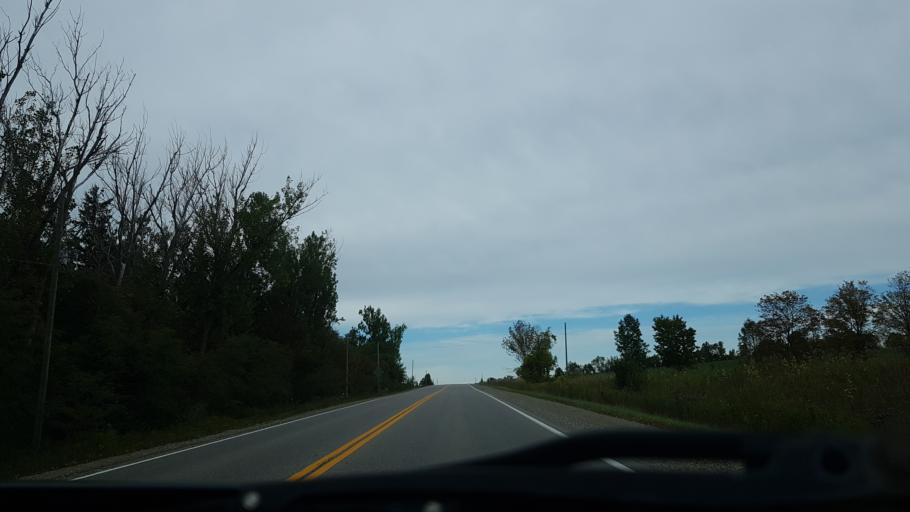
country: CA
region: Ontario
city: Shelburne
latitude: 44.0969
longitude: -80.0226
